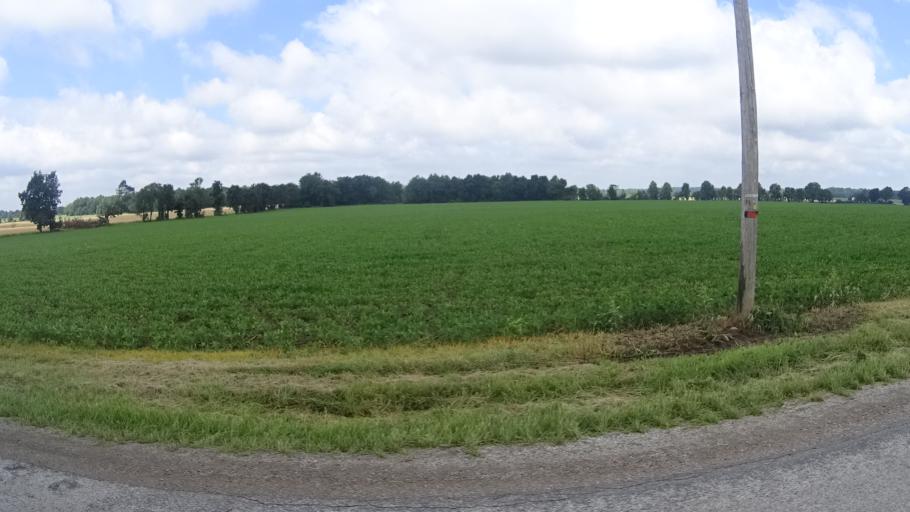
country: US
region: Ohio
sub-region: Huron County
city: Wakeman
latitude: 41.2995
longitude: -82.3874
